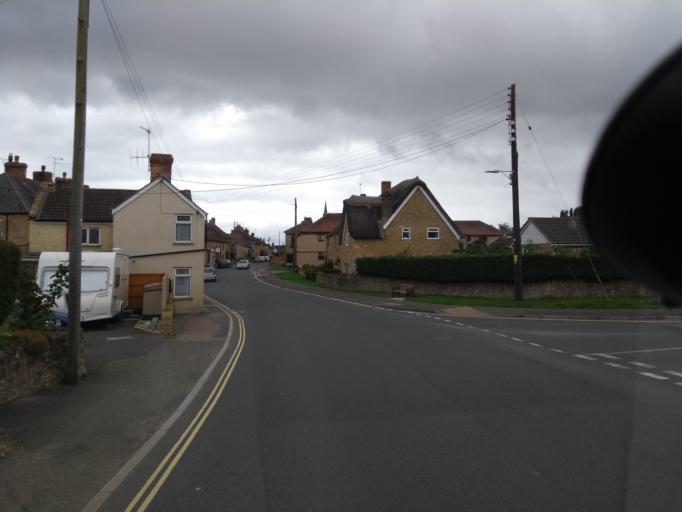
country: GB
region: England
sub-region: Somerset
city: Martock
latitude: 50.9759
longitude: -2.7673
